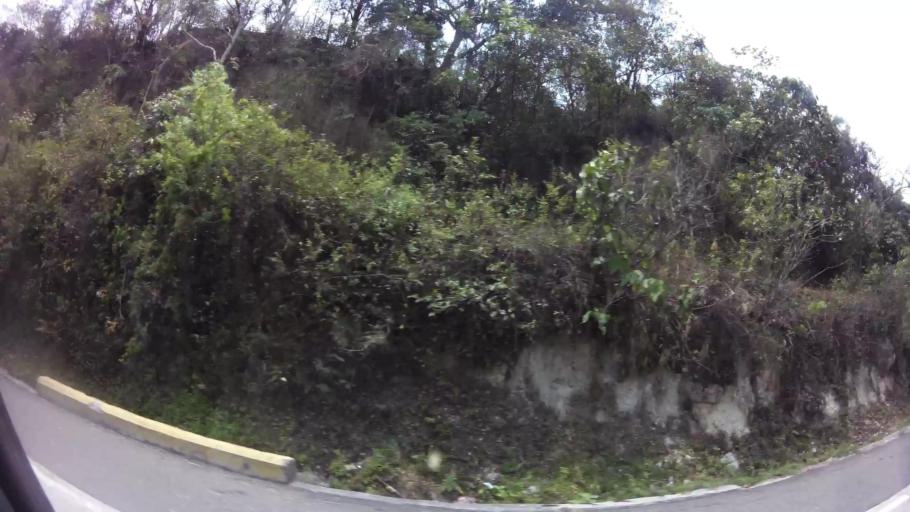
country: HN
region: Comayagua
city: Taulabe
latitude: 14.6839
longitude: -87.9501
